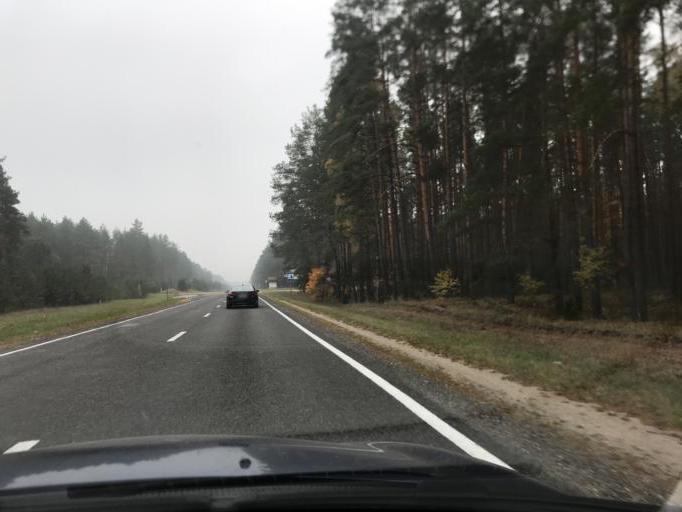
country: LT
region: Alytaus apskritis
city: Druskininkai
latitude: 53.8639
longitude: 23.8934
